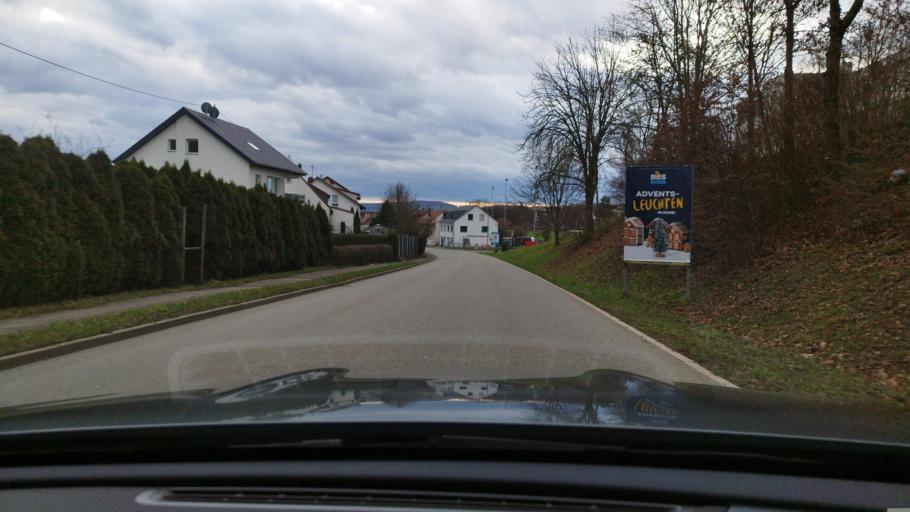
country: DE
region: Baden-Wuerttemberg
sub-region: Regierungsbezirk Stuttgart
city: Korb
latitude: 48.8474
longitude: 9.3568
